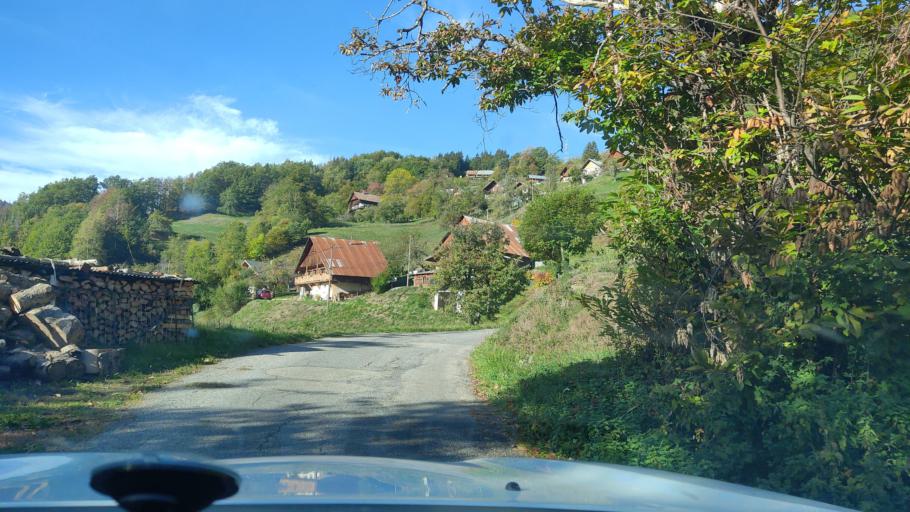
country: FR
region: Rhone-Alpes
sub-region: Departement de la Savoie
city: Marthod
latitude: 45.7198
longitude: 6.4791
